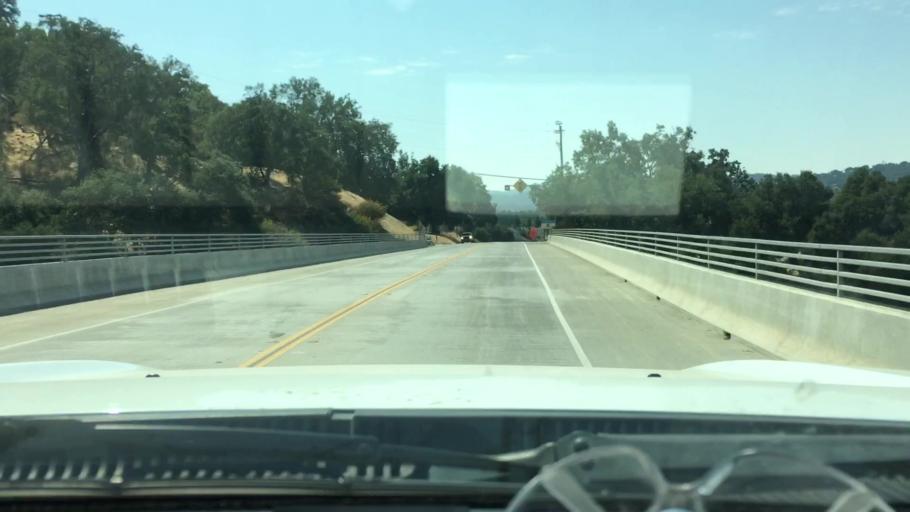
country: US
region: California
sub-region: San Luis Obispo County
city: Atascadero
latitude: 35.4913
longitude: -120.6624
